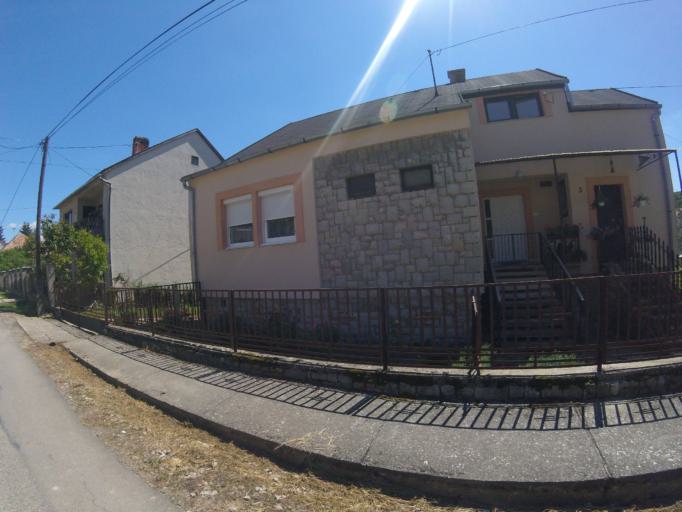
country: HU
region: Baranya
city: Sasd
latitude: 46.1431
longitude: 18.1171
